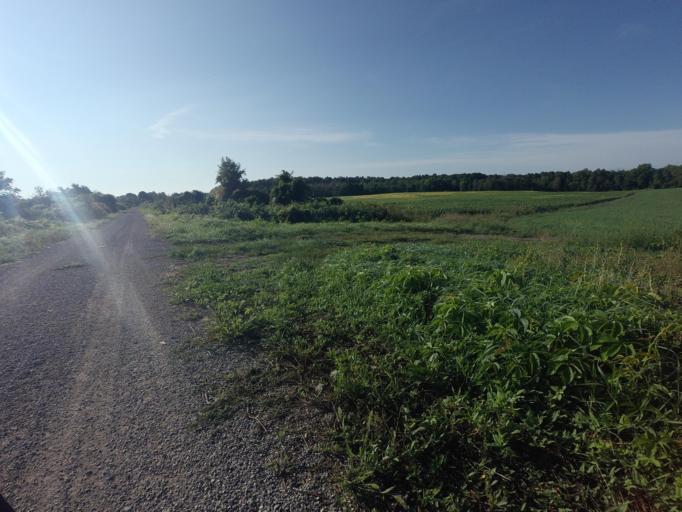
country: CA
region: Ontario
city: Goderich
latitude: 43.7535
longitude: -81.5089
